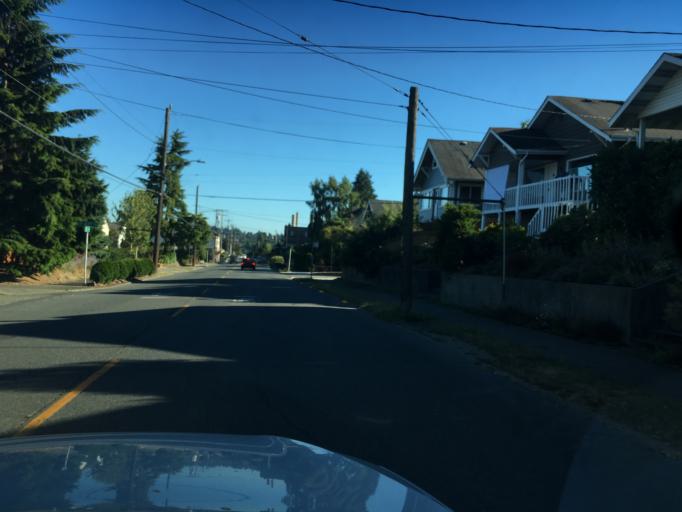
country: US
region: Washington
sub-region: King County
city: Shoreline
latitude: 47.6776
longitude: -122.3984
